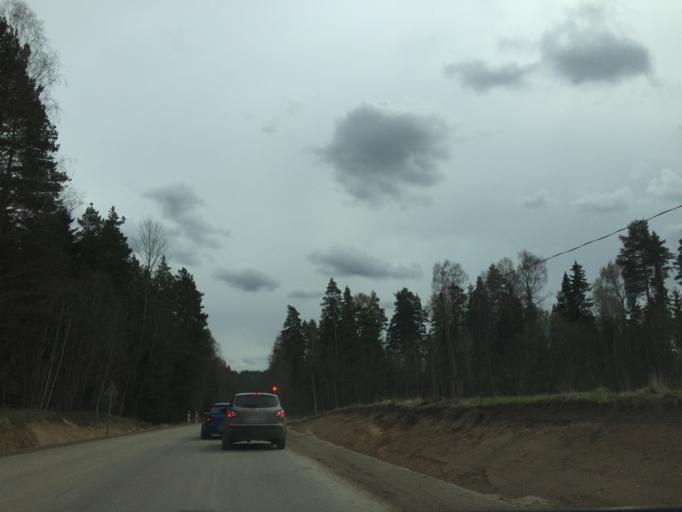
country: LV
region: Priekuli
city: Priekuli
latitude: 57.3129
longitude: 25.3794
